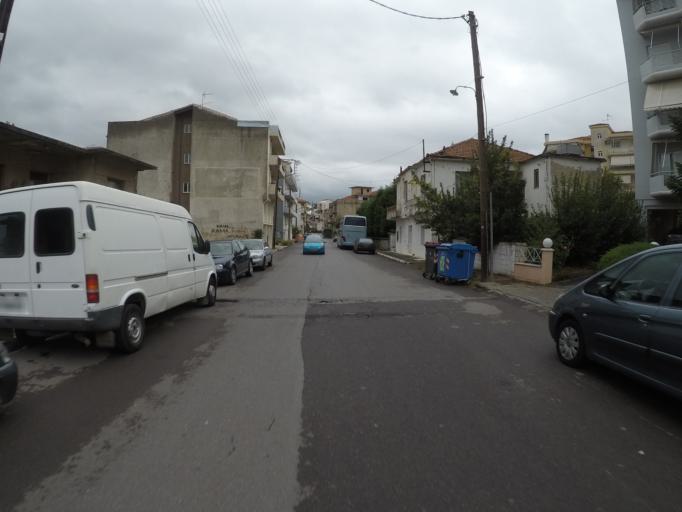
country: GR
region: Peloponnese
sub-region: Nomos Arkadias
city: Tripoli
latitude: 37.5184
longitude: 22.3755
